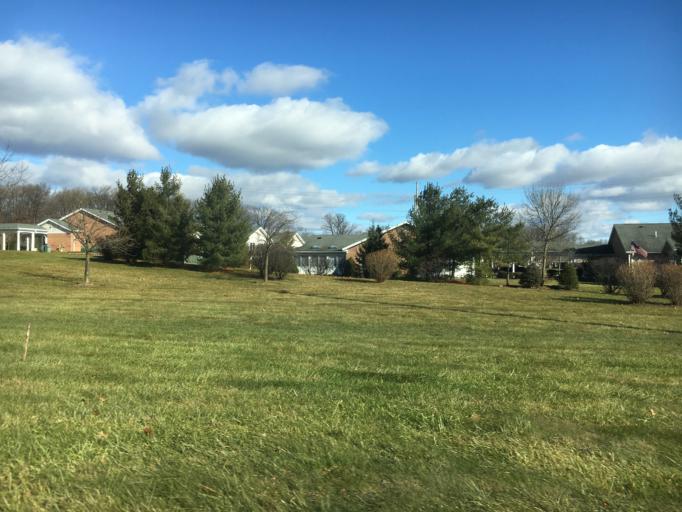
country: US
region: Pennsylvania
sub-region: Lehigh County
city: Stiles
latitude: 40.6401
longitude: -75.5125
